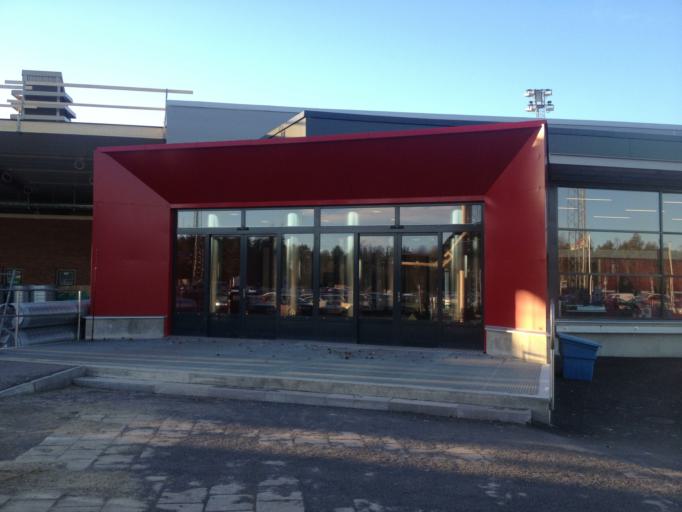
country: SE
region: Vaesterbotten
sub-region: Umea Kommun
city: Umea
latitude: 63.7931
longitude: 20.2905
